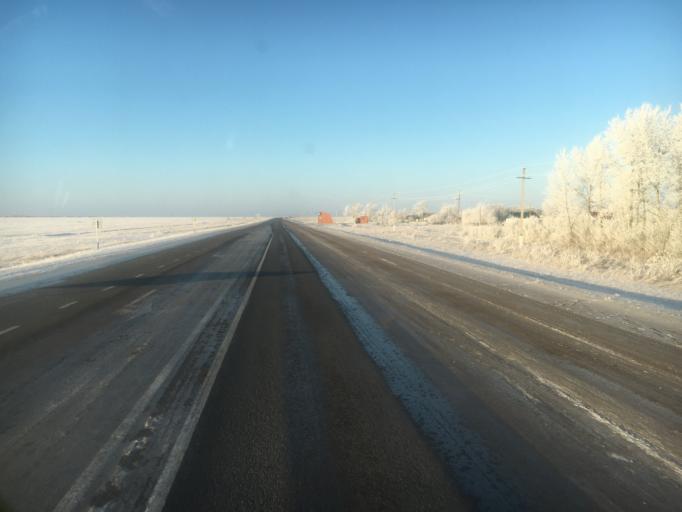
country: KZ
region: Soltustik Qazaqstan
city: Taiynsha
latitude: 53.7507
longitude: 69.3623
